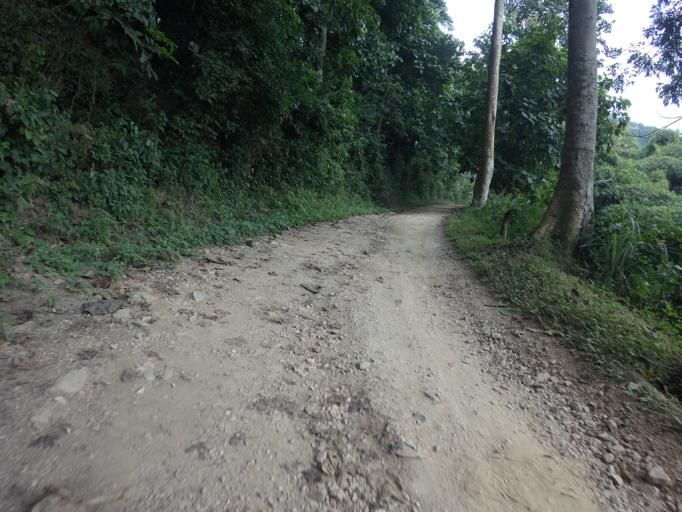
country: GH
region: Volta
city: Kpandu
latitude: 6.8800
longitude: 0.4385
